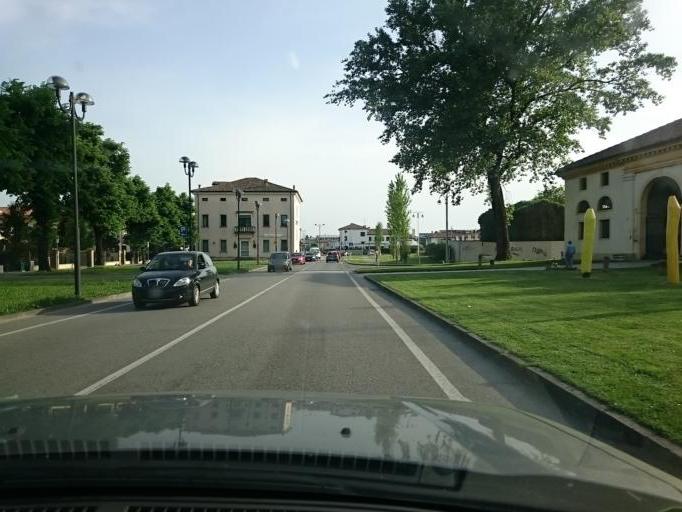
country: IT
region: Veneto
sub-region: Provincia di Padova
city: Noventa
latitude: 45.4133
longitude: 11.9501
